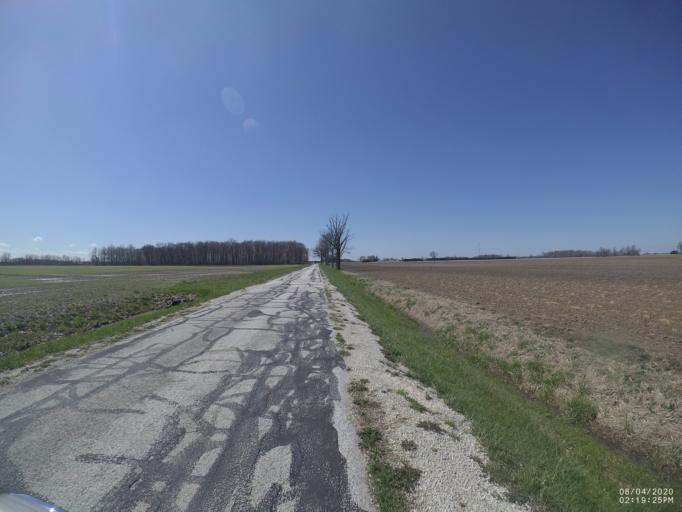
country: US
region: Ohio
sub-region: Sandusky County
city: Stony Prairie
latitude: 41.2894
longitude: -83.2412
